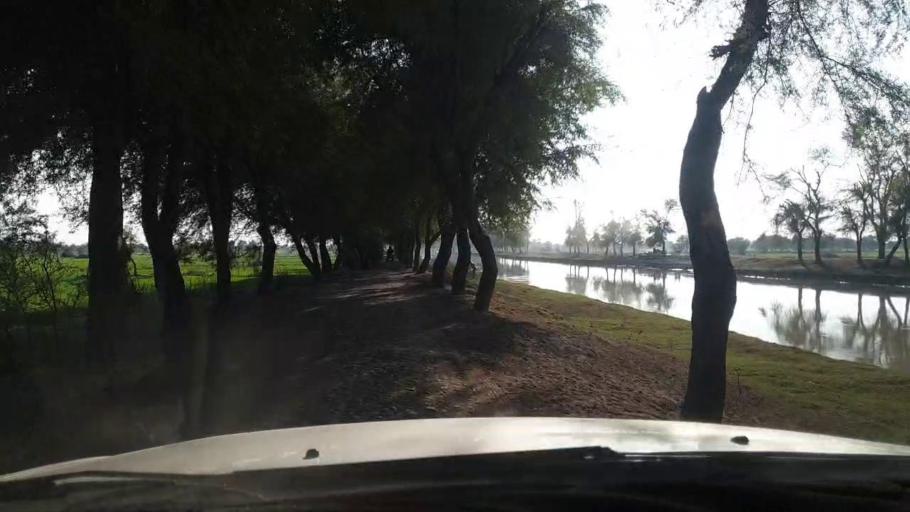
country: PK
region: Sindh
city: Mirpur Mathelo
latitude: 27.9701
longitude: 69.5239
